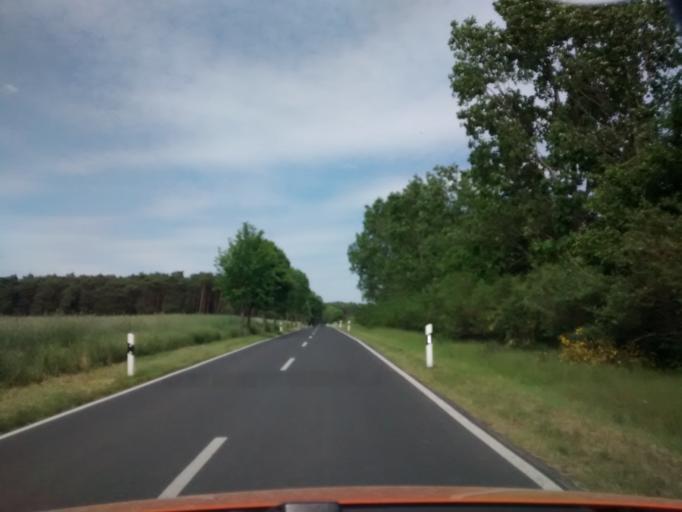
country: DE
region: Brandenburg
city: Ihlow
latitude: 51.9043
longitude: 13.3164
